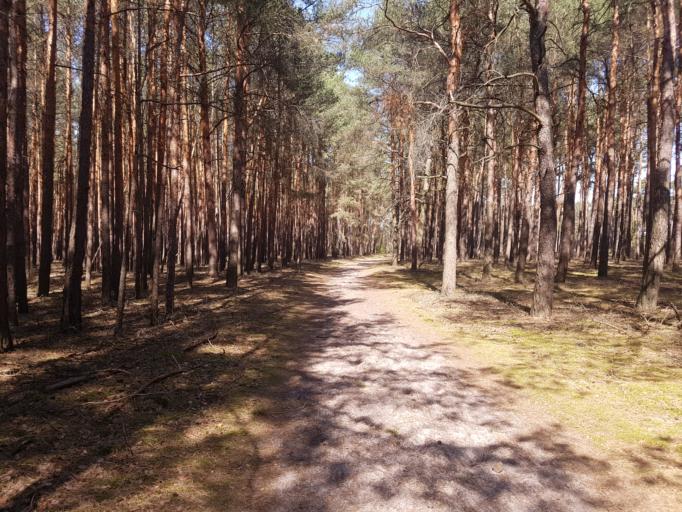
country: DE
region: Brandenburg
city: Bruck
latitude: 52.1746
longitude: 12.7570
